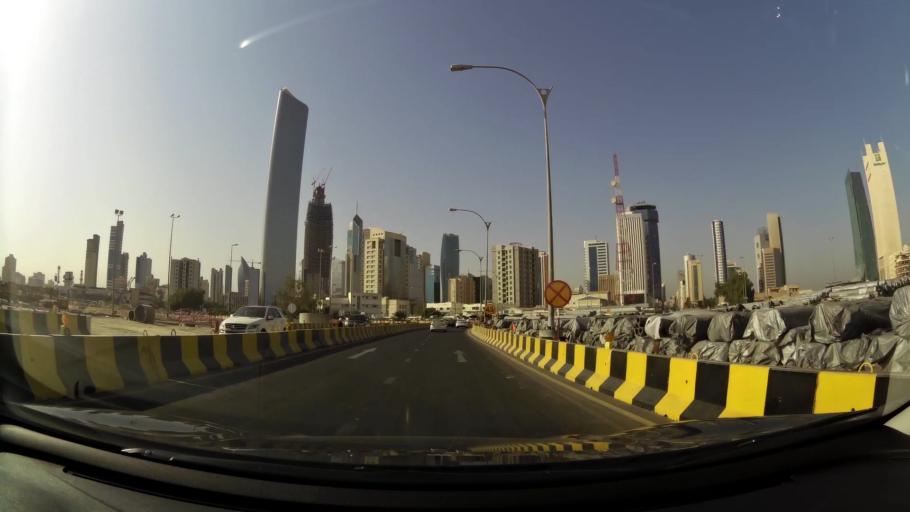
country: KW
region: Al Asimah
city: Ad Dasmah
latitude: 29.3864
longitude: 47.9948
